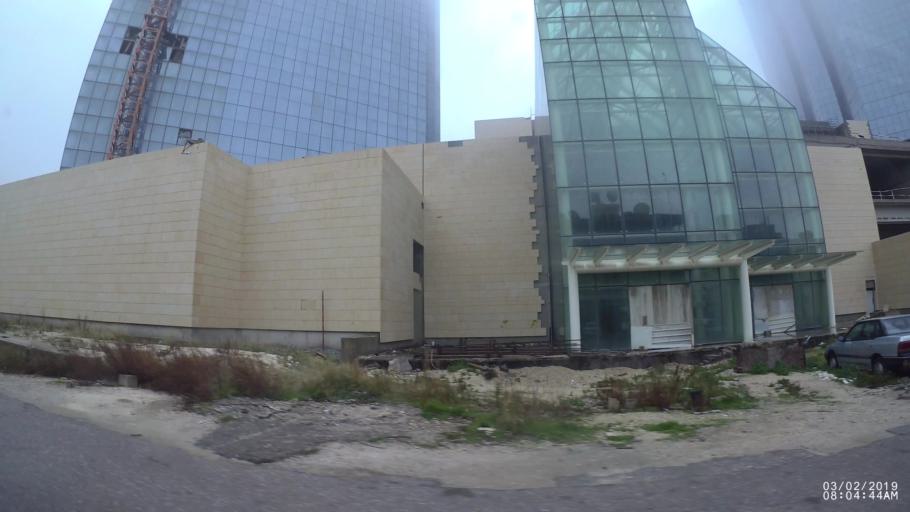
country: JO
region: Amman
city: Wadi as Sir
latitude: 31.9627
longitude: 35.8683
